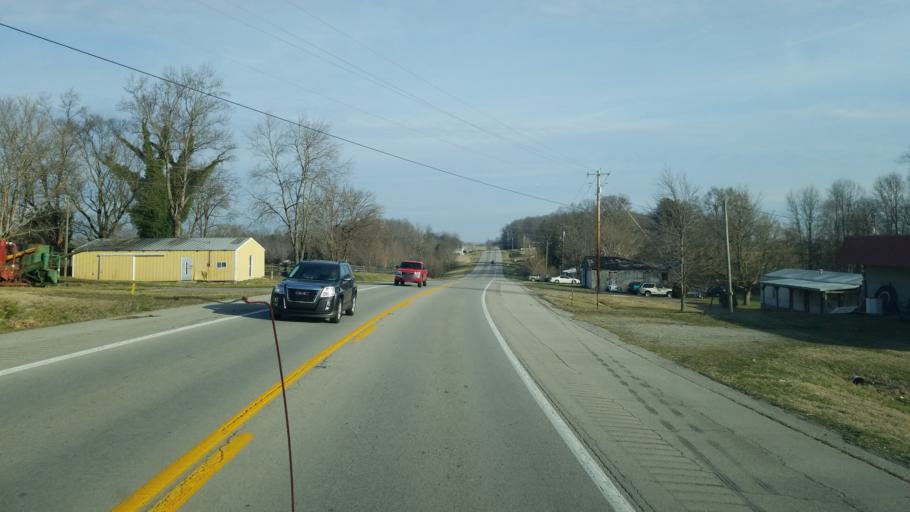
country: US
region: Kentucky
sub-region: Russell County
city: Russell Springs
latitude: 37.0757
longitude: -85.0713
